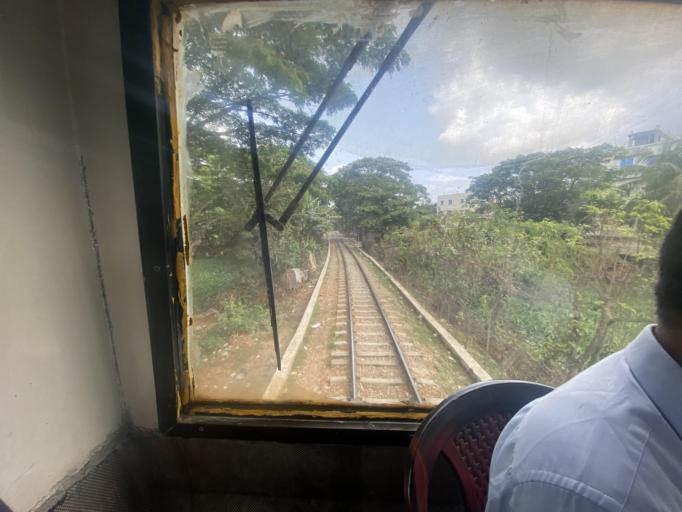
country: BD
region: Chittagong
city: Chittagong
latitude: 22.3310
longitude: 91.7729
